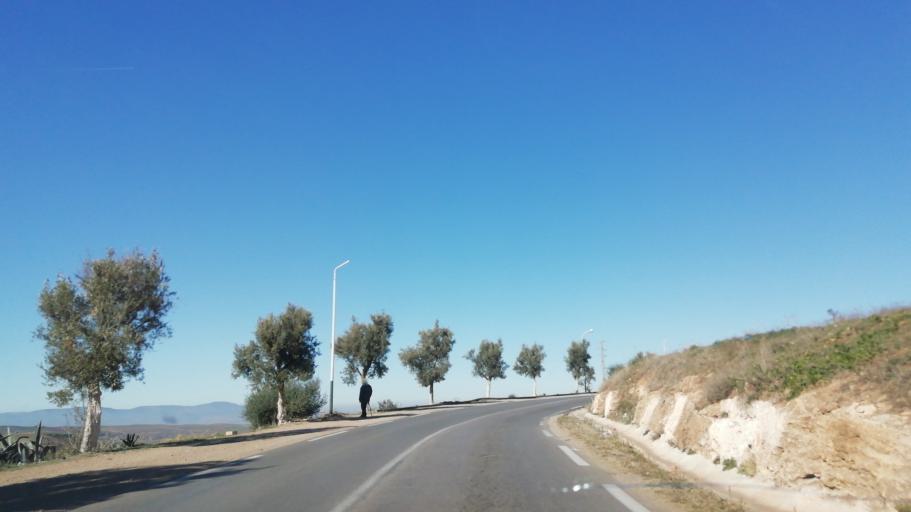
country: DZ
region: Tlemcen
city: Beni Mester
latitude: 34.8416
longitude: -1.4763
